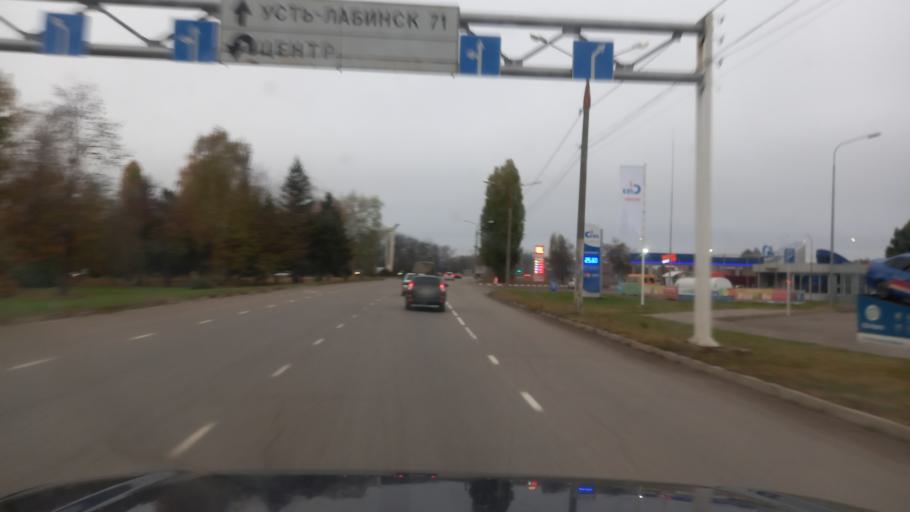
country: RU
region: Adygeya
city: Maykop
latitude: 44.6231
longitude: 40.0573
